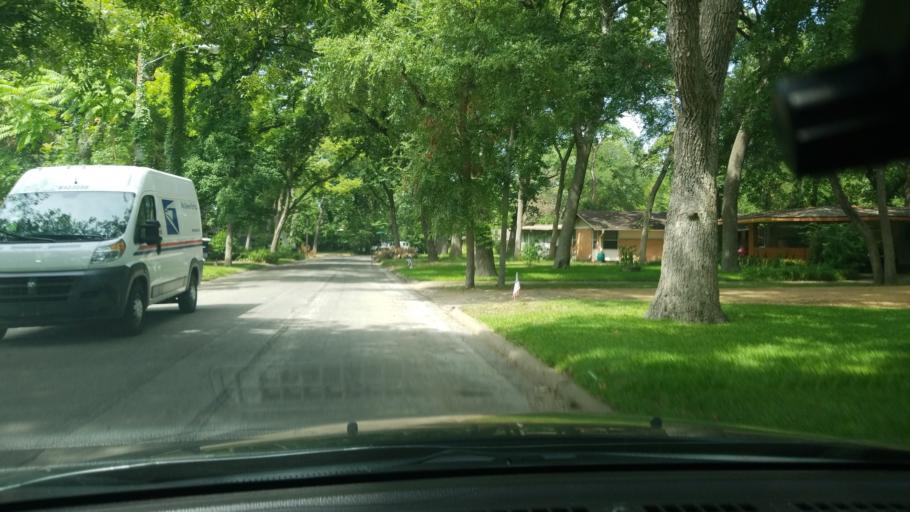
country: US
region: Texas
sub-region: Dallas County
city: Highland Park
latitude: 32.8146
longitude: -96.7071
